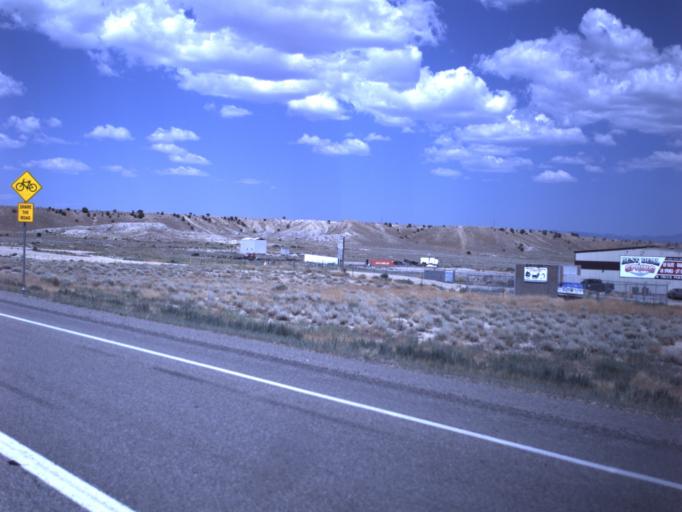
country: US
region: Utah
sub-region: Carbon County
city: Price
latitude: 39.5369
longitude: -110.8153
